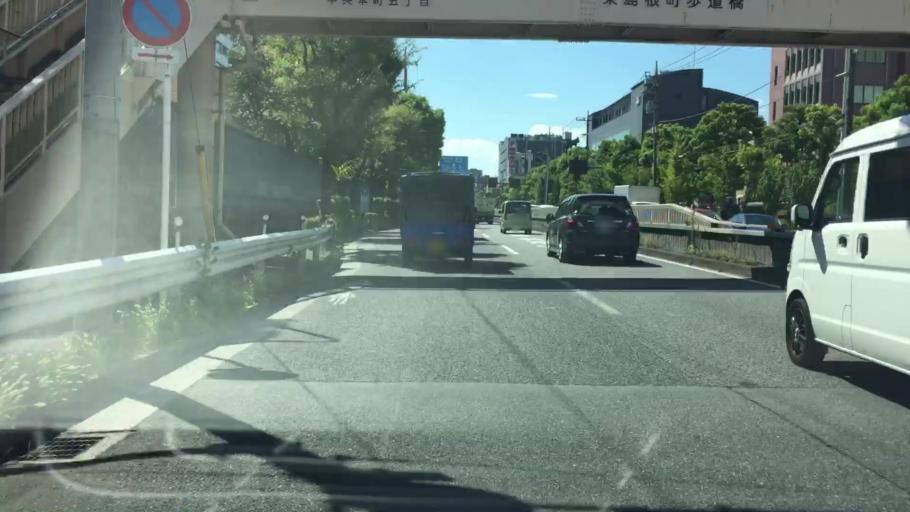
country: JP
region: Saitama
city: Soka
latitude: 35.7786
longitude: 139.8110
